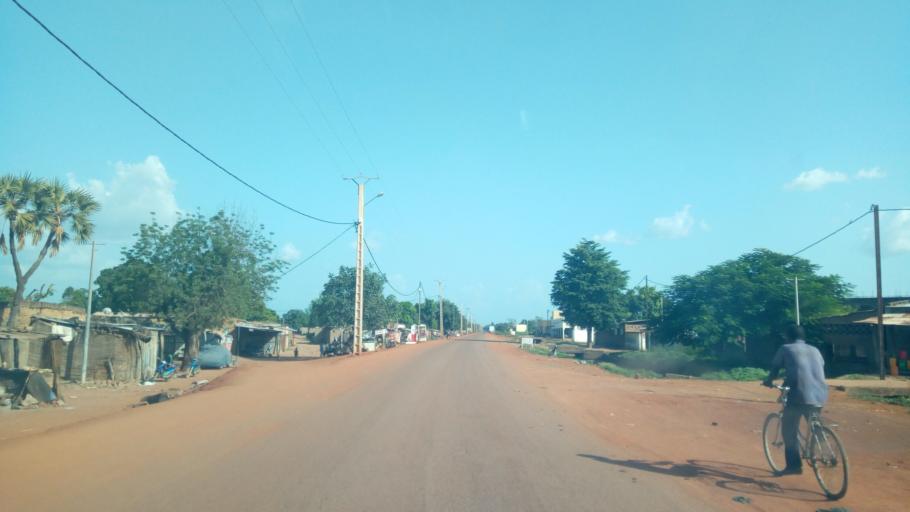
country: ML
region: Sikasso
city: Yorosso
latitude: 12.1816
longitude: -4.8015
